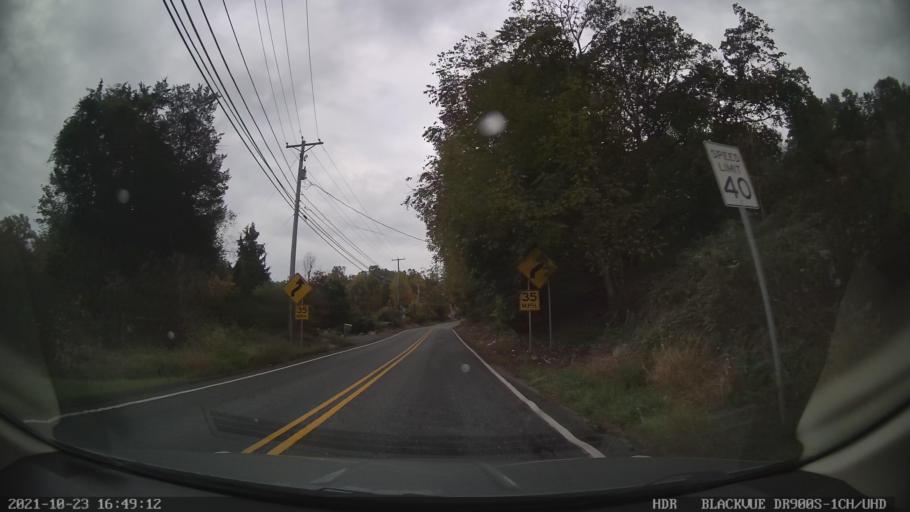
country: US
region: Pennsylvania
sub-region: Berks County
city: Red Lion
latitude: 40.4884
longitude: -75.6144
